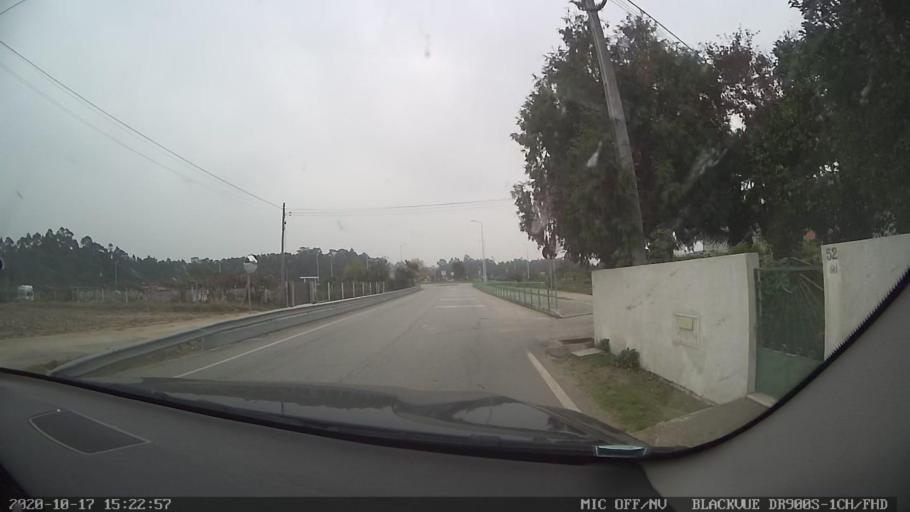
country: PT
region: Braga
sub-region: Esposende
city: Esposende
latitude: 41.5311
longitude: -8.7372
